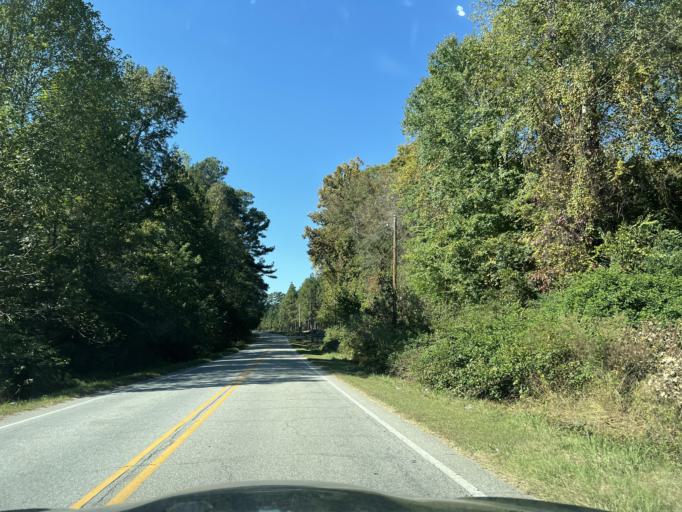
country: US
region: North Carolina
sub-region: Johnston County
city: Clayton
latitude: 35.6737
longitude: -78.4875
